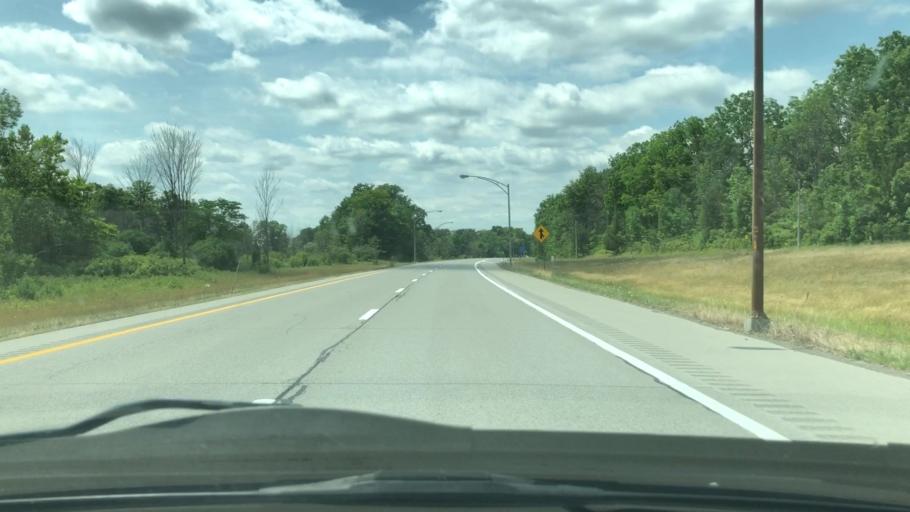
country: US
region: New York
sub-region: Monroe County
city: Churchville
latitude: 43.0957
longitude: -77.7999
